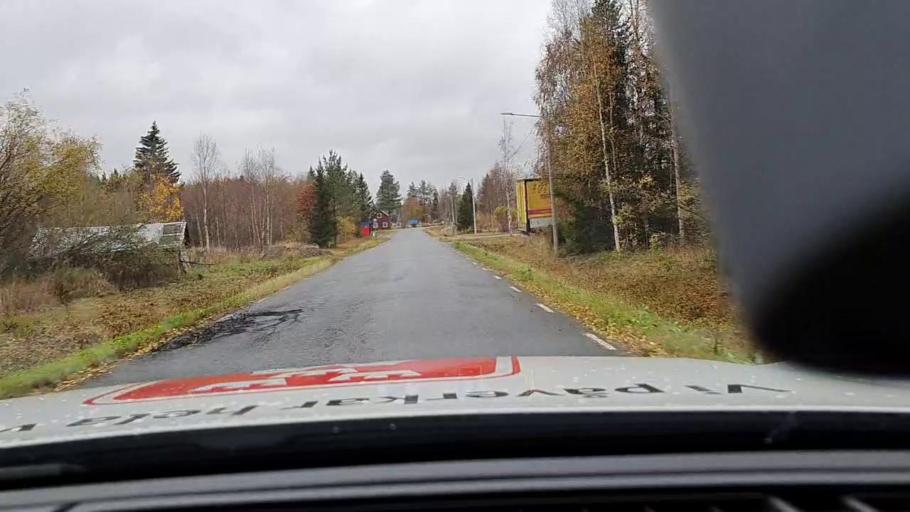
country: SE
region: Norrbotten
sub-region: Haparanda Kommun
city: Haparanda
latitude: 65.9462
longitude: 23.7991
